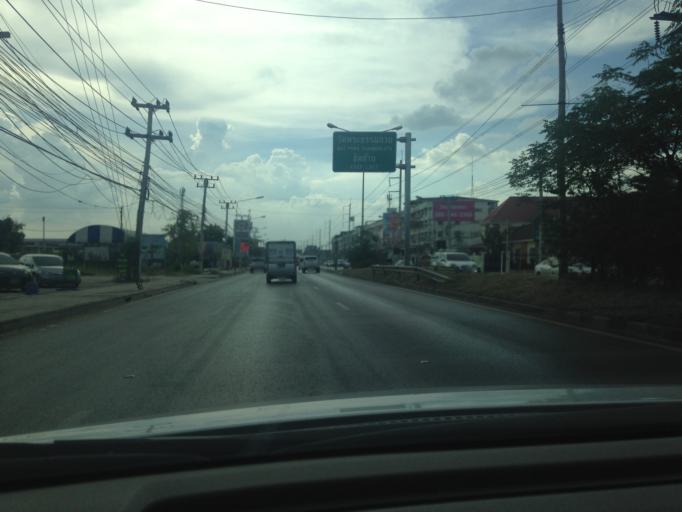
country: TH
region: Pathum Thani
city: Khlong Luang
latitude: 14.0656
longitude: 100.6529
